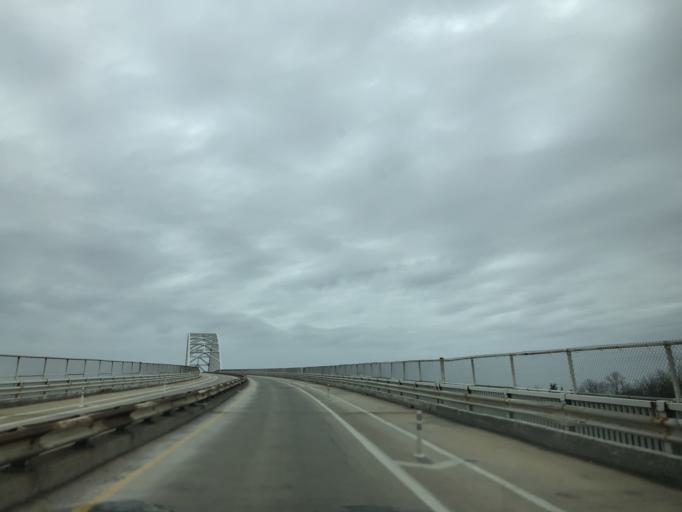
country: US
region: Delaware
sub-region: New Castle County
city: Delaware City
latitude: 39.5493
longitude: -75.6490
